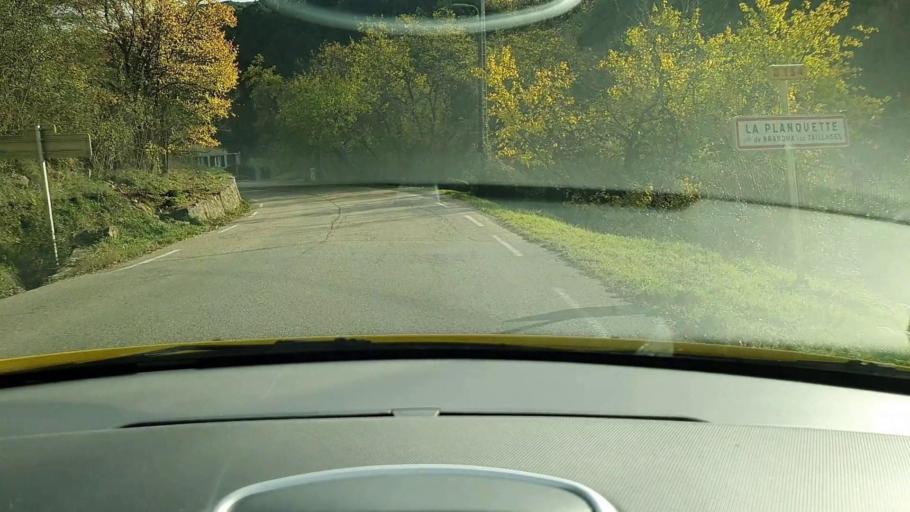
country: FR
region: Languedoc-Roussillon
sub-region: Departement du Gard
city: Branoux-les-Taillades
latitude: 44.2172
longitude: 4.0058
